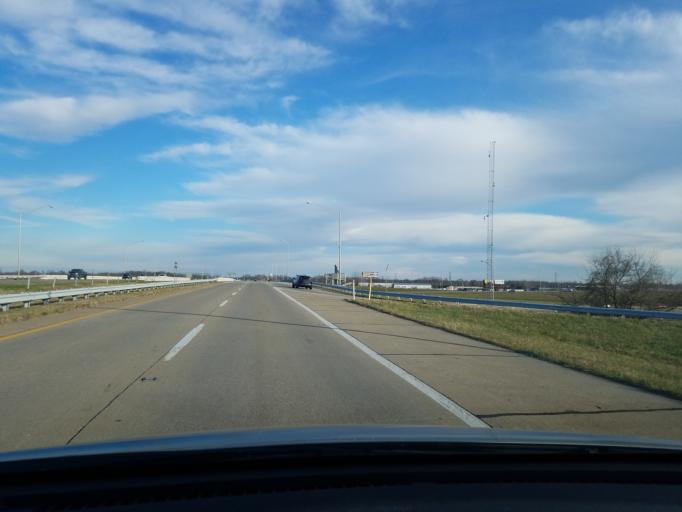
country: US
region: Indiana
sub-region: Clark County
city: Clarksville
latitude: 38.3456
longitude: -85.7558
